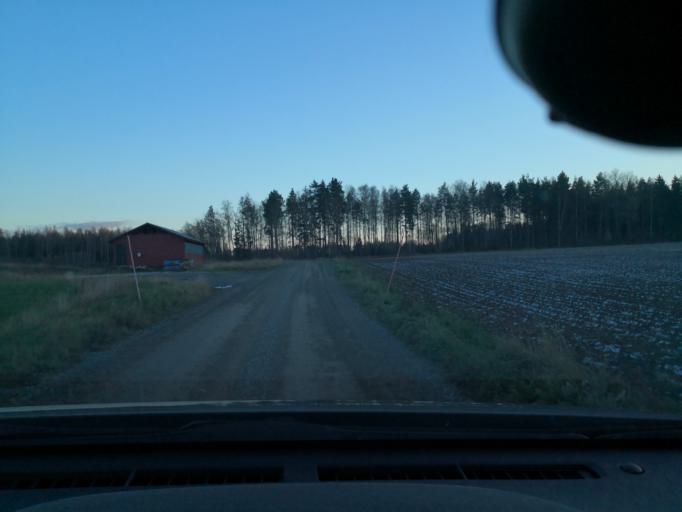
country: SE
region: Vaestmanland
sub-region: Vasteras
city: Tillberga
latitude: 59.7696
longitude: 16.6015
